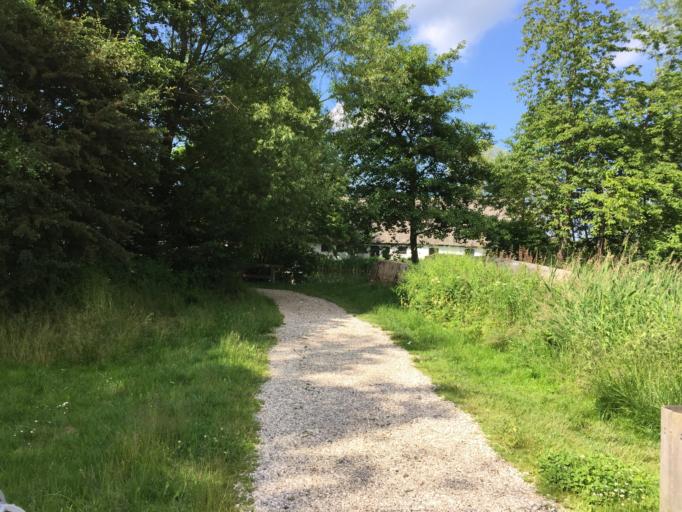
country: DK
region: Capital Region
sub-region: Hillerod Kommune
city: Nodebo
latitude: 56.0455
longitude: 12.3773
